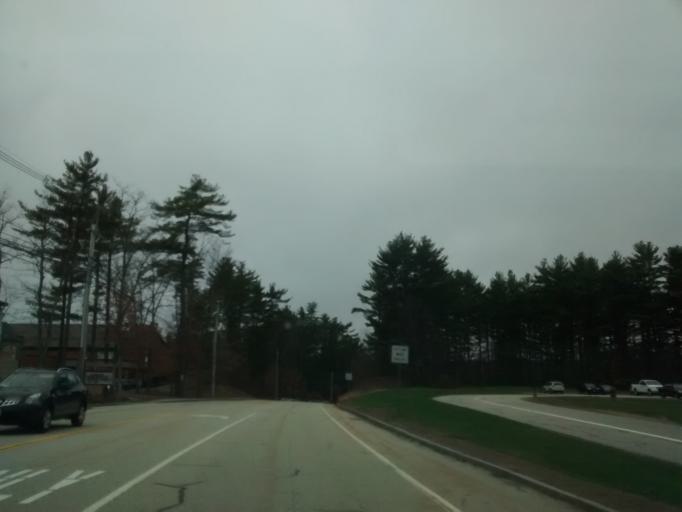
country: US
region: Massachusetts
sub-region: Worcester County
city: Upton
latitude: 42.1609
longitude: -71.6164
